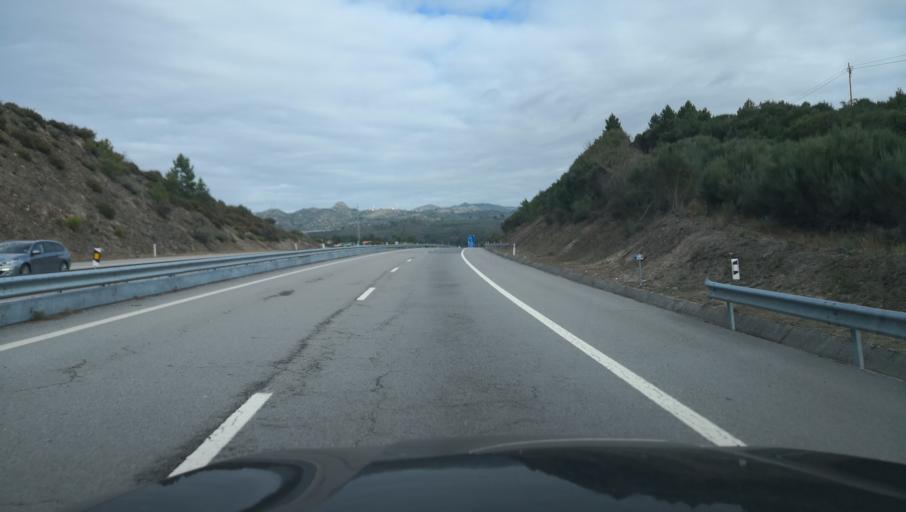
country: PT
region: Vila Real
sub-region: Vila Real
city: Vila Real
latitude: 41.3451
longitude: -7.7044
